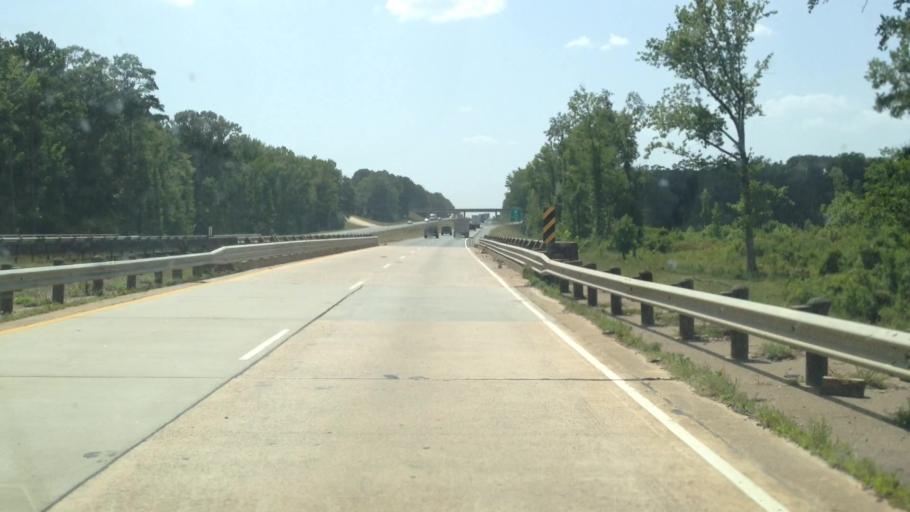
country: US
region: Louisiana
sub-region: Webster Parish
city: Minden
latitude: 32.5621
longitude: -93.1519
